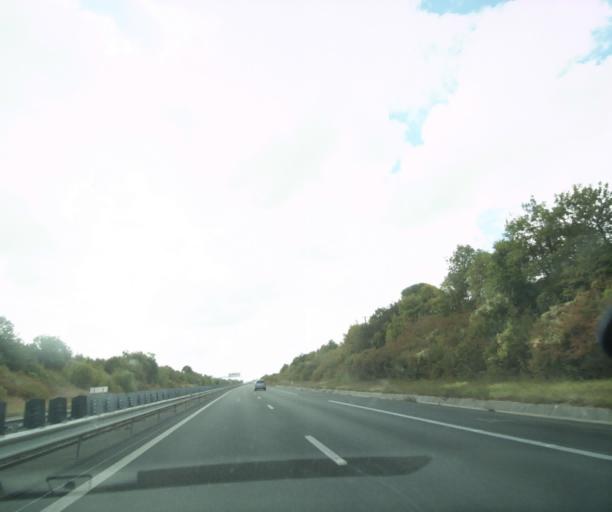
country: FR
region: Poitou-Charentes
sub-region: Departement de la Charente-Maritime
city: Saintes
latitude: 45.7290
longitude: -0.6622
